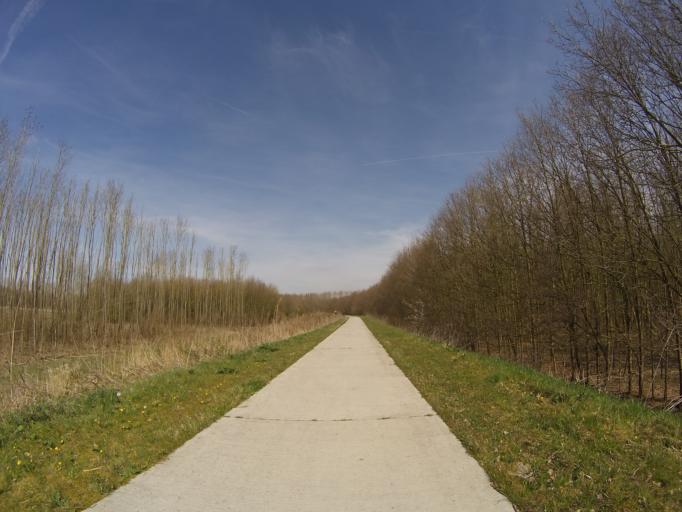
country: NL
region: Flevoland
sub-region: Gemeente Zeewolde
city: Zeewolde
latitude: 52.3121
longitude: 5.4694
